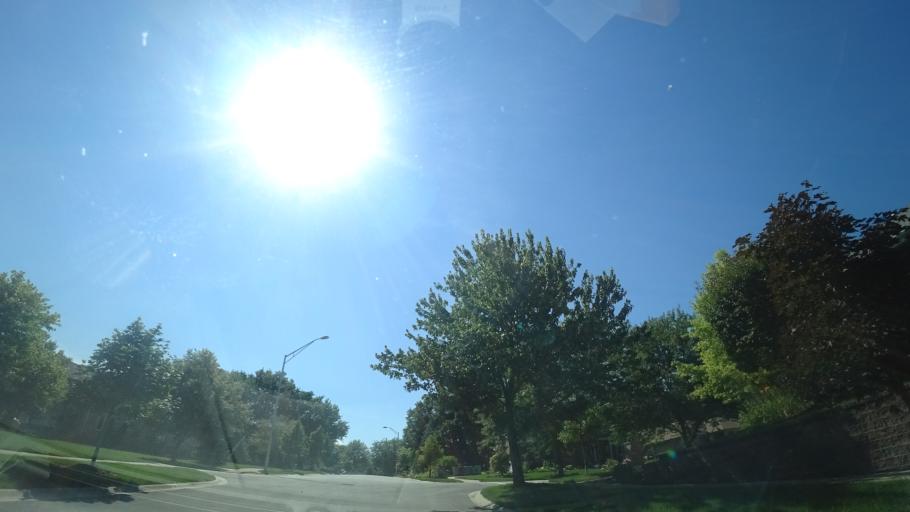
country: US
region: Illinois
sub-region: Will County
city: Mokena
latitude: 41.5678
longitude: -87.9023
